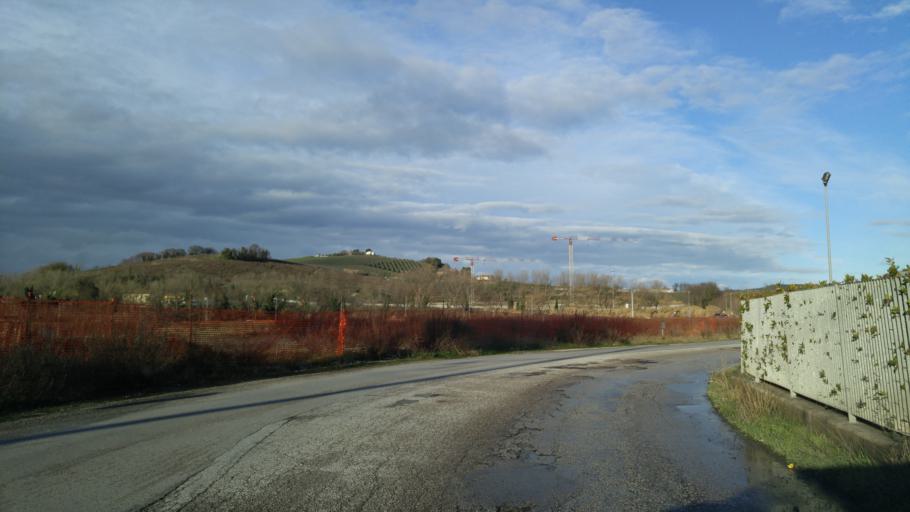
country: IT
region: The Marches
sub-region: Provincia di Ancona
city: San Biagio
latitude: 43.5295
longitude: 13.5211
